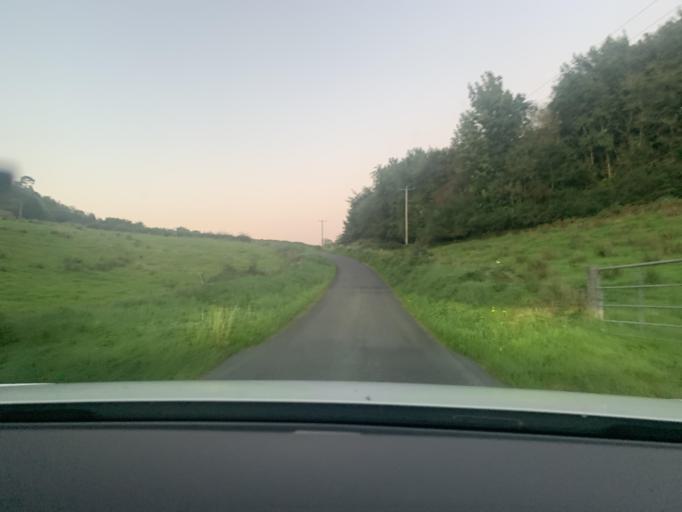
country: IE
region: Connaught
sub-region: County Leitrim
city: Manorhamilton
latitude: 54.2608
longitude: -8.2964
